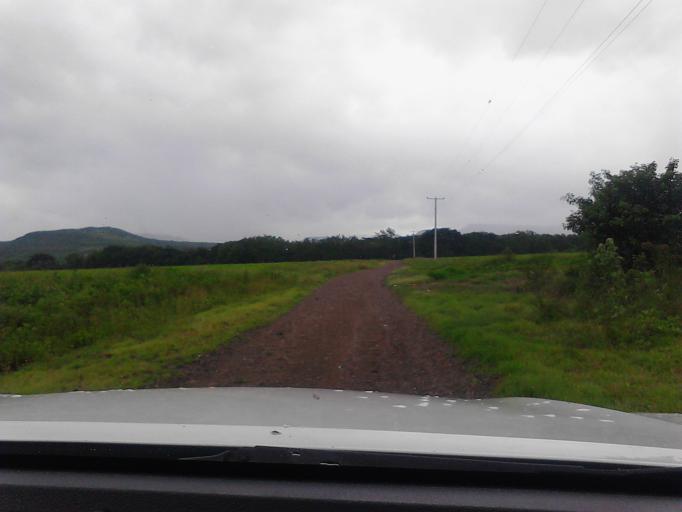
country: NI
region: Matagalpa
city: Ciudad Dario
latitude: 12.9018
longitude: -86.1353
